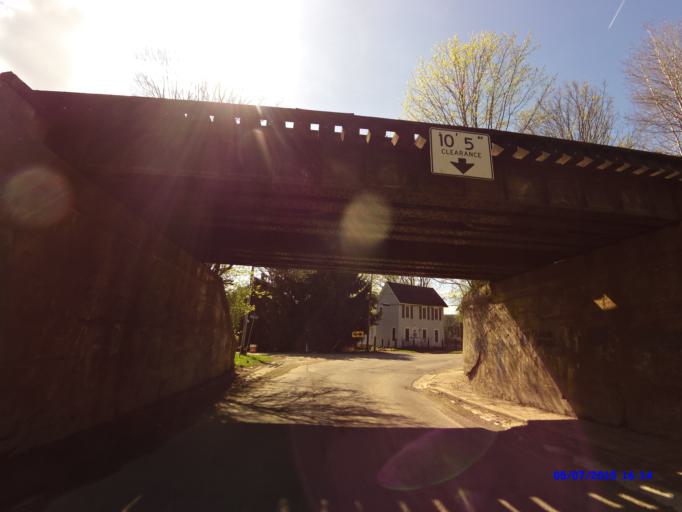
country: US
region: New York
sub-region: Cattaraugus County
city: Salamanca
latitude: 42.2733
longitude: -78.6655
